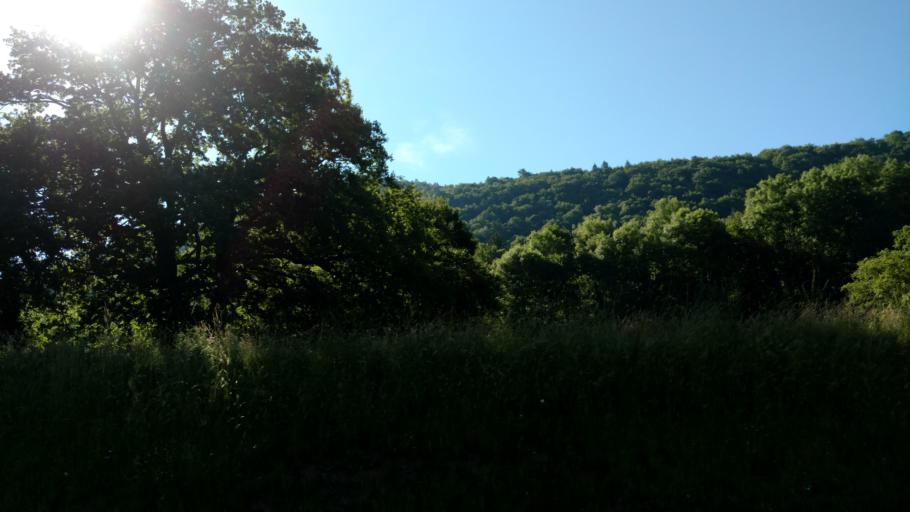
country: FR
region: Rhone-Alpes
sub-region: Departement de la Haute-Savoie
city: Margencel
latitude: 46.3256
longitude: 6.4445
